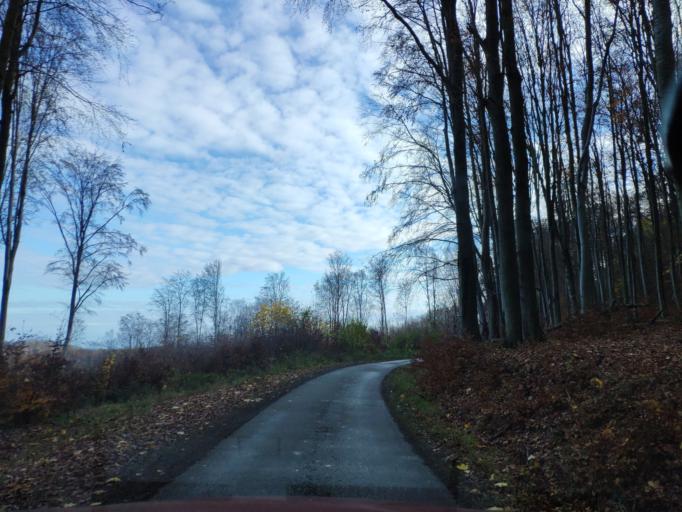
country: HU
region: Borsod-Abauj-Zemplen
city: Gonc
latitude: 48.5862
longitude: 21.4684
